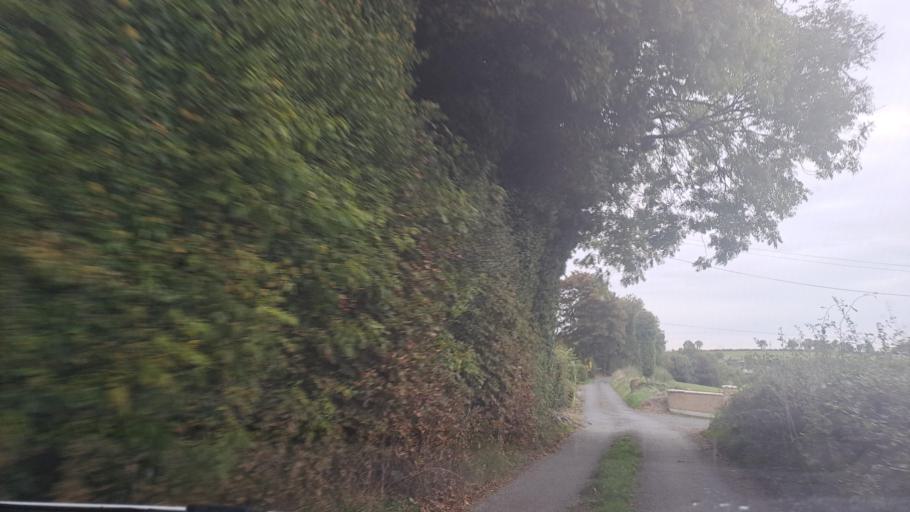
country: IE
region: Ulster
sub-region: County Monaghan
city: Carrickmacross
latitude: 53.9825
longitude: -6.7786
